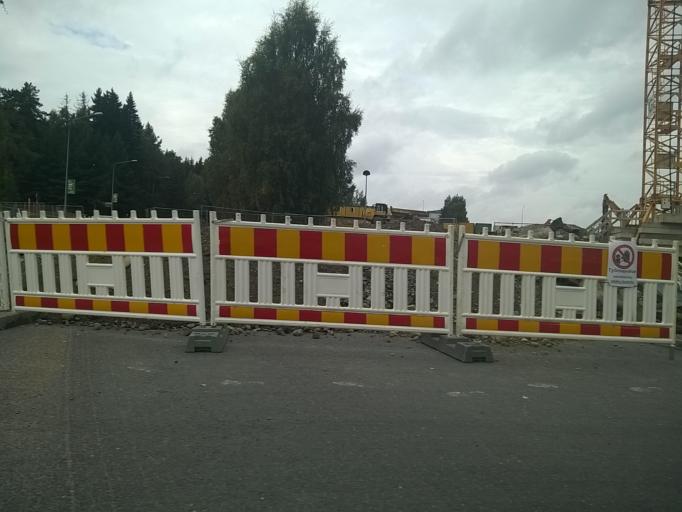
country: FI
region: Pirkanmaa
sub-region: Tampere
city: Tampere
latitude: 61.4924
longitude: 23.8167
